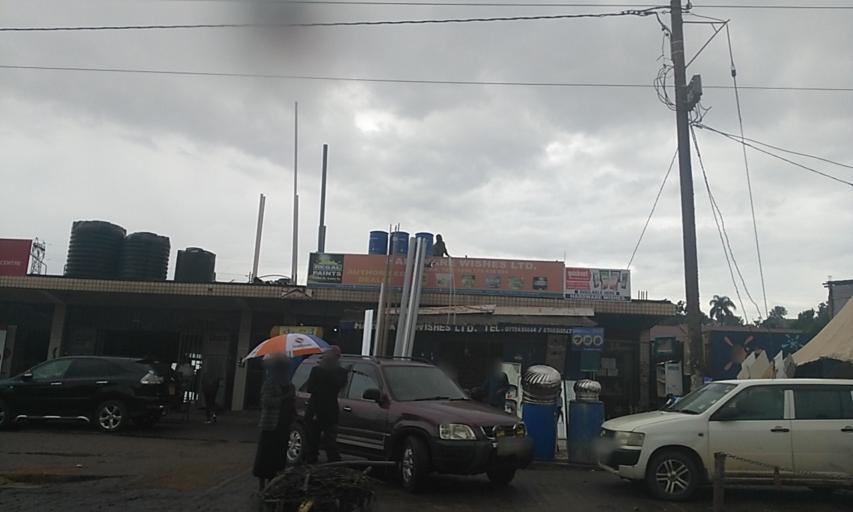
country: UG
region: Central Region
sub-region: Wakiso District
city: Kireka
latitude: 0.3454
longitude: 32.6448
